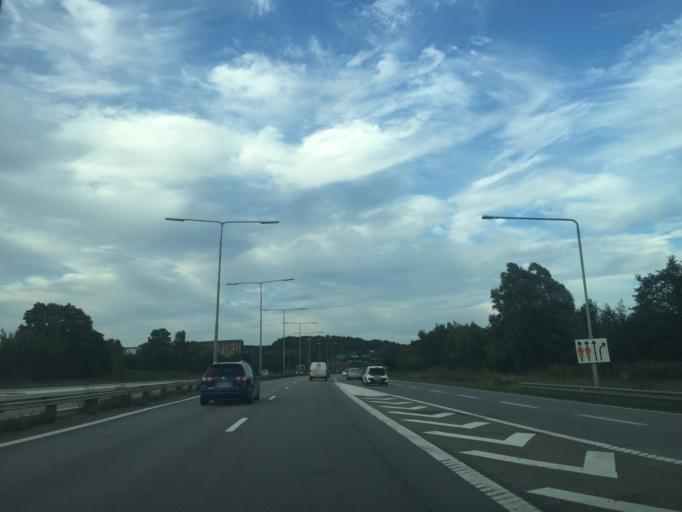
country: SE
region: Vaestra Goetaland
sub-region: Goteborg
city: Goeteborg
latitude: 57.7246
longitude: 11.9622
